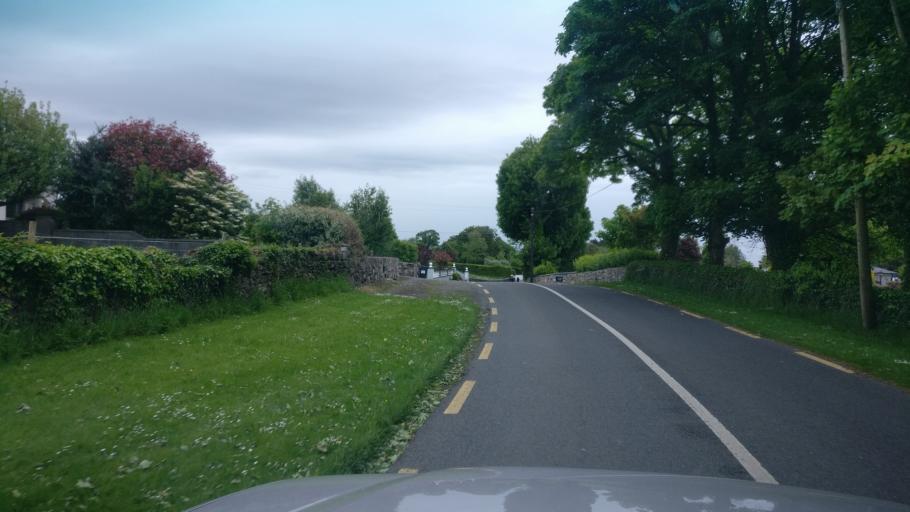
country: IE
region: Connaught
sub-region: County Galway
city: Loughrea
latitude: 53.0905
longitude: -8.4633
